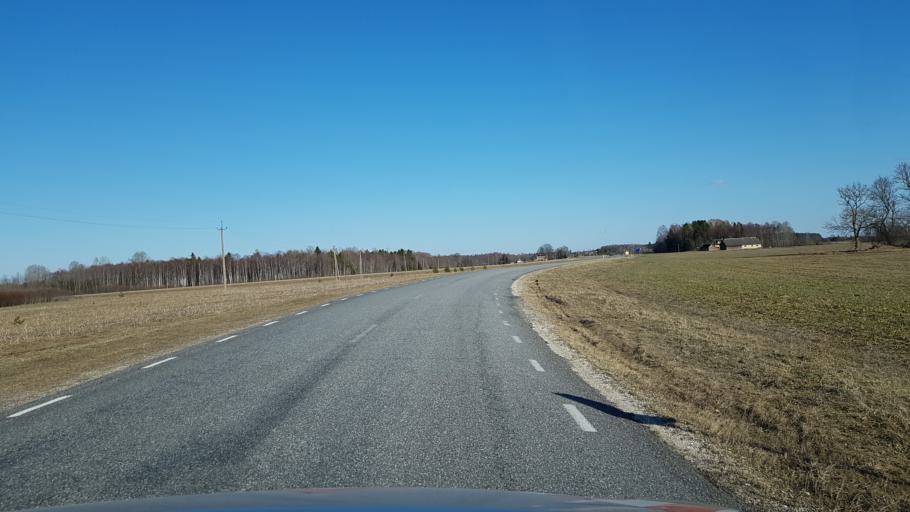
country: EE
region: Laeaene-Virumaa
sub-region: Haljala vald
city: Haljala
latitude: 59.4637
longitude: 26.1915
